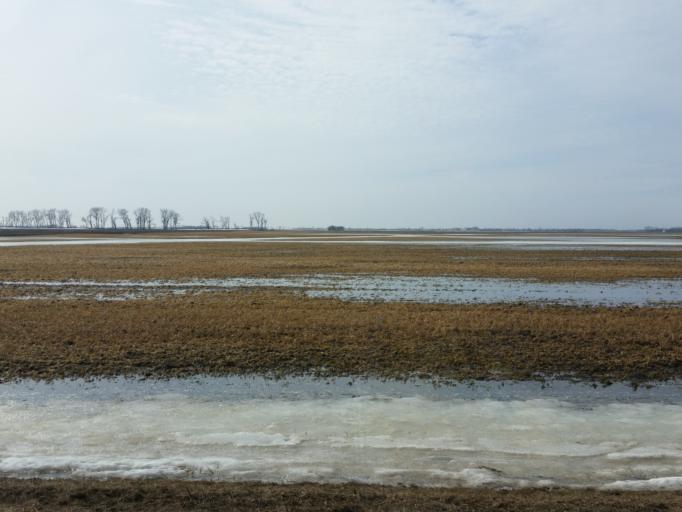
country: US
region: North Dakota
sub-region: Walsh County
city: Grafton
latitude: 48.4202
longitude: -97.2122
